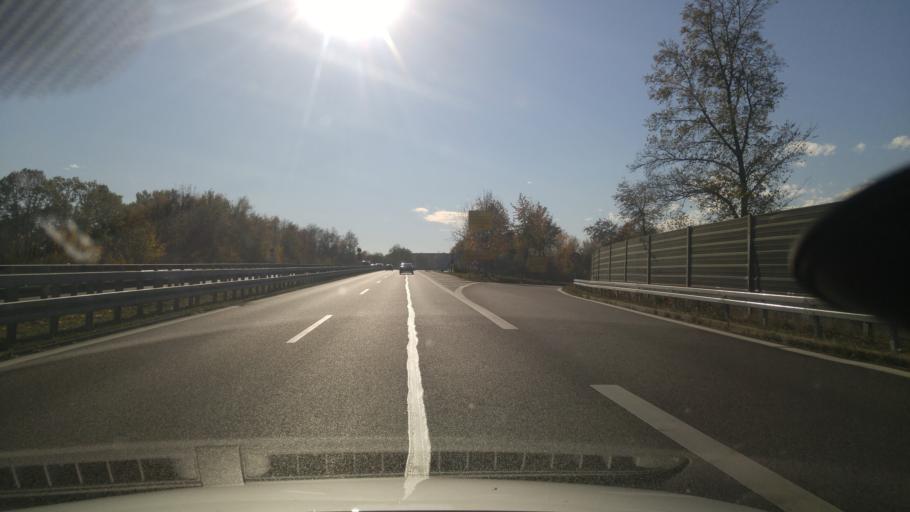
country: DE
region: Baden-Wuerttemberg
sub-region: Regierungsbezirk Stuttgart
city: Kongen
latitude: 48.6773
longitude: 9.3696
